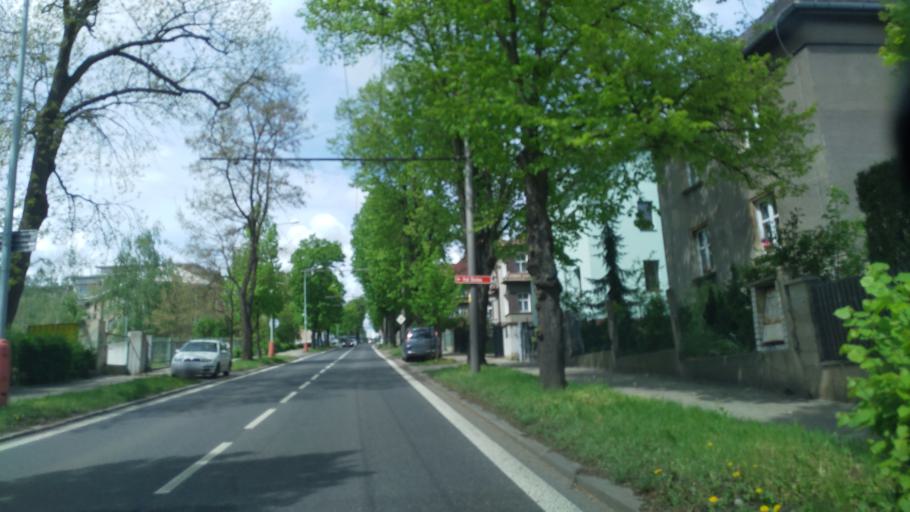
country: CZ
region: Ustecky
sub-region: Okres Usti nad Labem
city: Usti nad Labem
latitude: 50.6687
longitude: 14.0352
